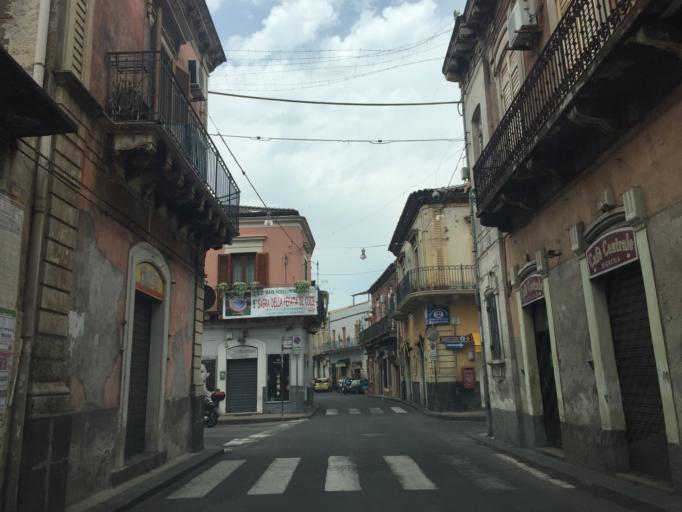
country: IT
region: Sicily
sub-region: Catania
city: Aci Castello
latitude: 37.5548
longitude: 15.1463
